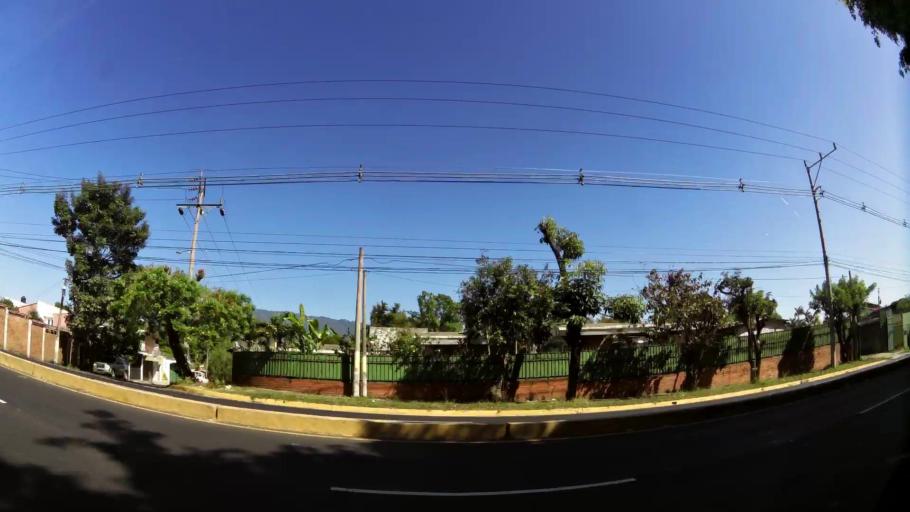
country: SV
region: La Libertad
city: Santa Tecla
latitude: 13.6664
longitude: -89.2837
